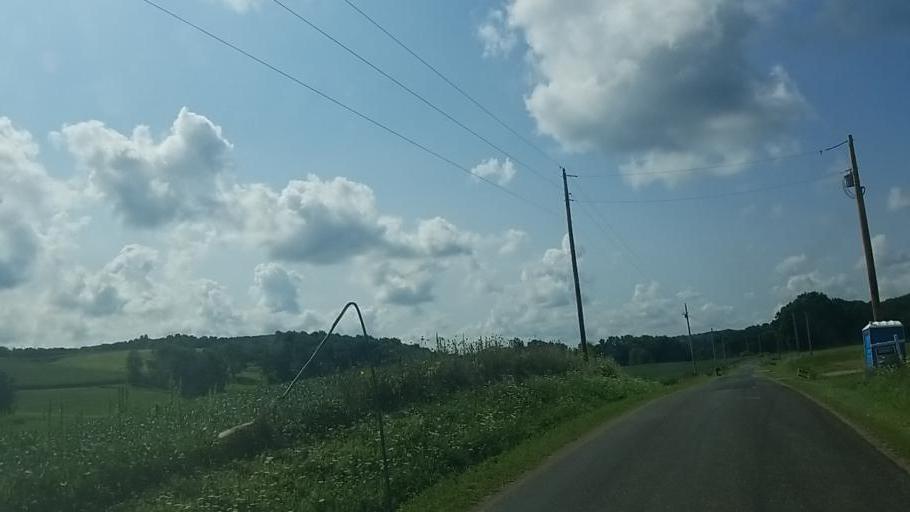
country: US
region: Ohio
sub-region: Ashland County
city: Ashland
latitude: 40.7546
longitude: -82.2995
